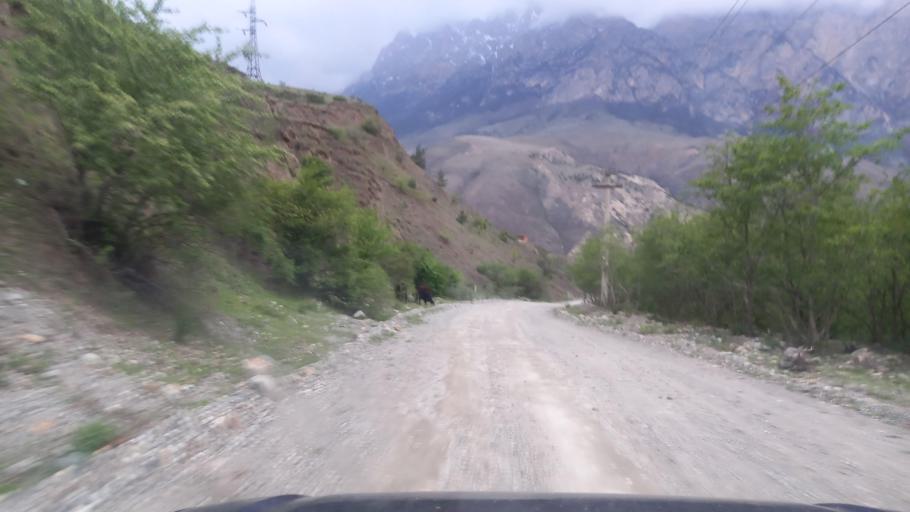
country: RU
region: North Ossetia
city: Mizur
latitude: 42.8528
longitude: 44.1536
